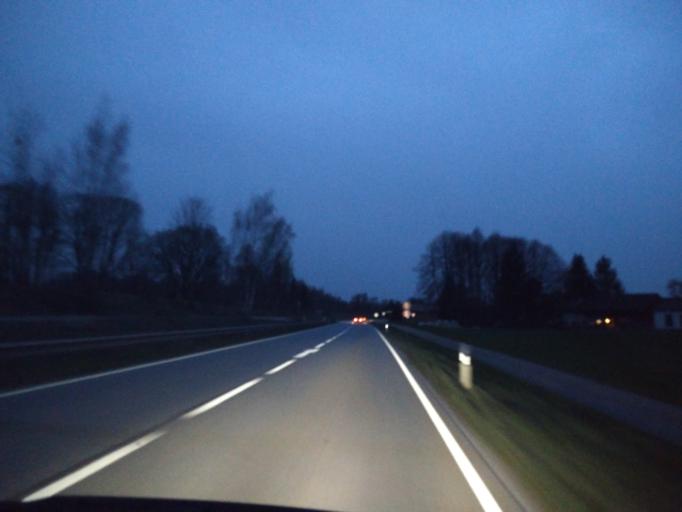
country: DE
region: Bavaria
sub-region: Upper Bavaria
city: Griesstatt
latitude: 48.0129
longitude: 12.1722
